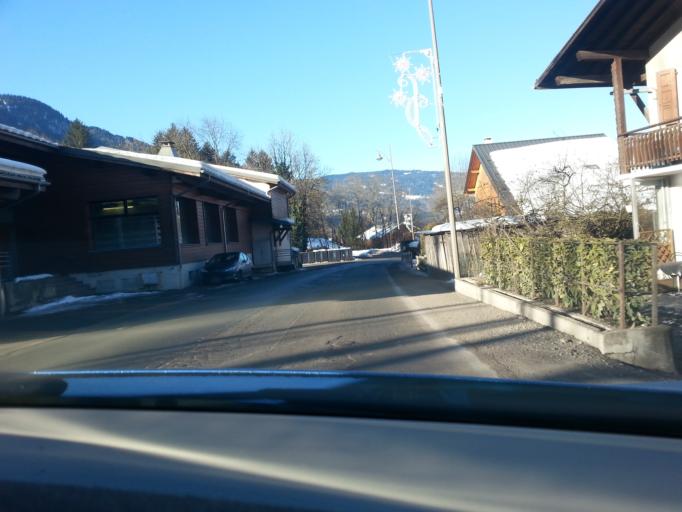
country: FR
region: Rhone-Alpes
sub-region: Departement de la Haute-Savoie
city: Samoens
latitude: 46.0801
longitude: 6.7300
